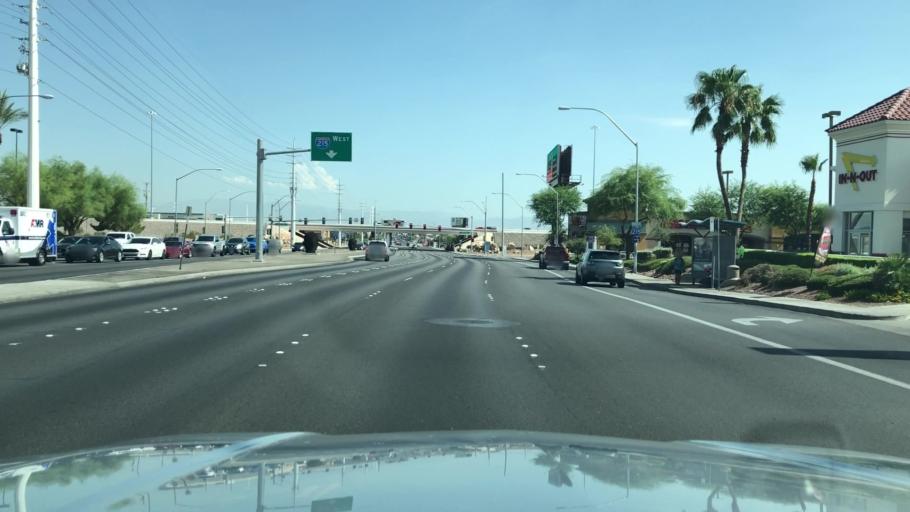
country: US
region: Nevada
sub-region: Clark County
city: Whitney
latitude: 36.0210
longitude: -115.1185
